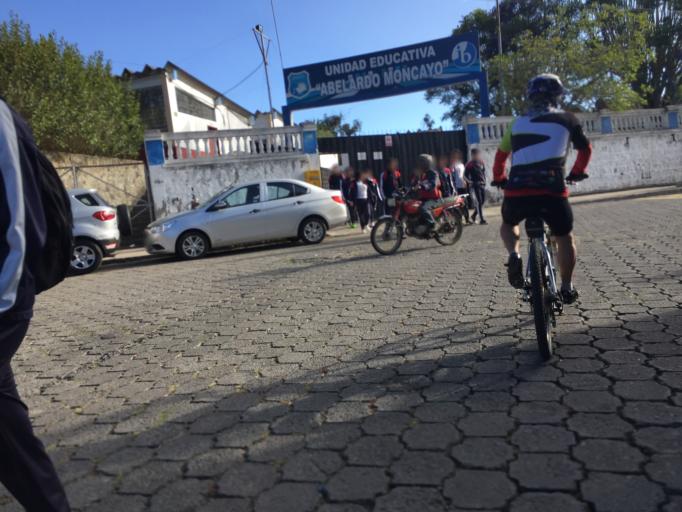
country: EC
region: Imbabura
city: Atuntaqui
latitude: 0.3393
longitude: -78.2067
